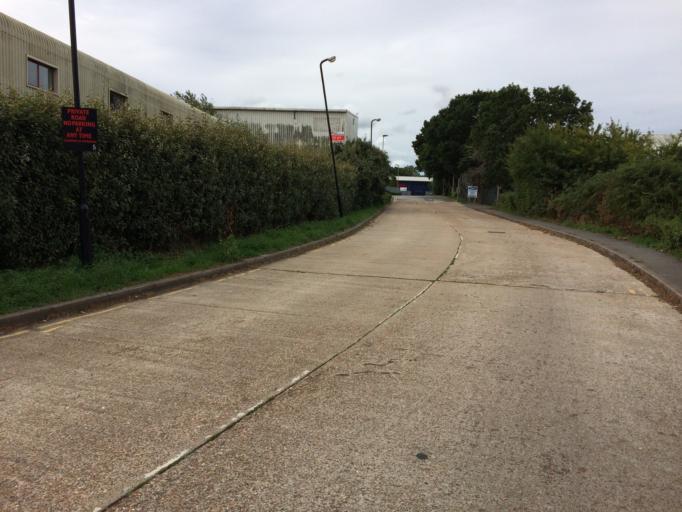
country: GB
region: England
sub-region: East Sussex
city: Hailsham
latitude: 50.8607
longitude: 0.2497
